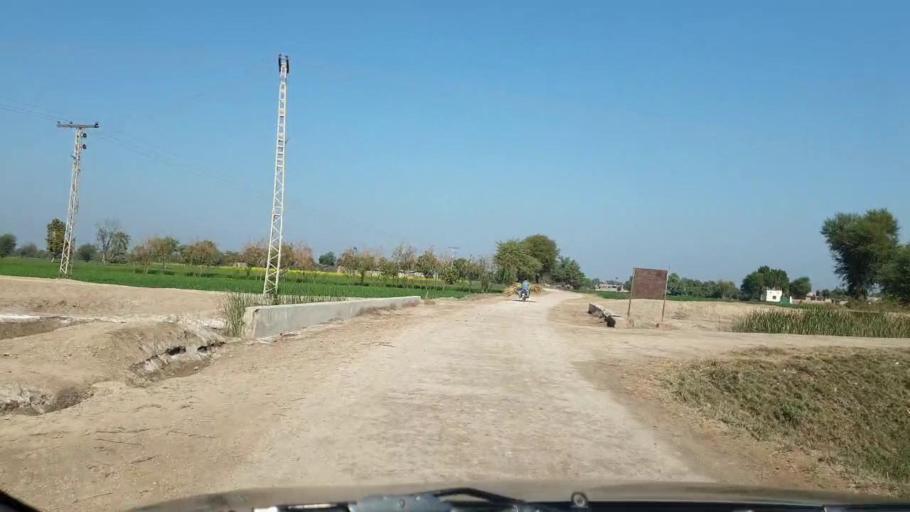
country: PK
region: Sindh
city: Sinjhoro
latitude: 25.9466
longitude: 68.7630
